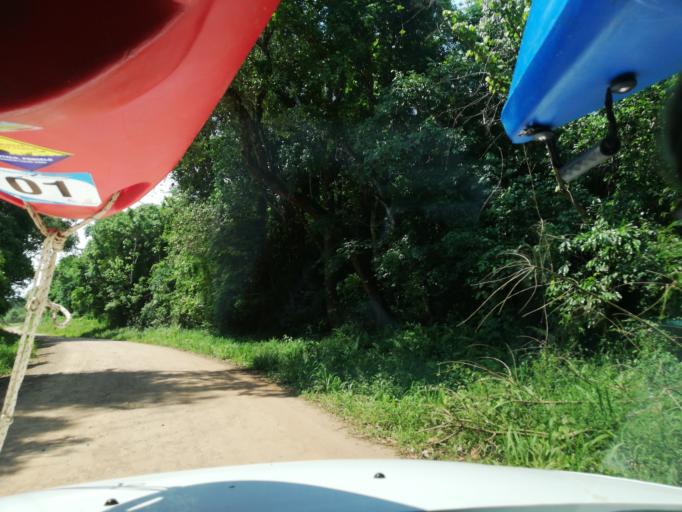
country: AR
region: Misiones
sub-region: Departamento de San Ignacio
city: San Ignacio
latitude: -27.2691
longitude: -55.5535
